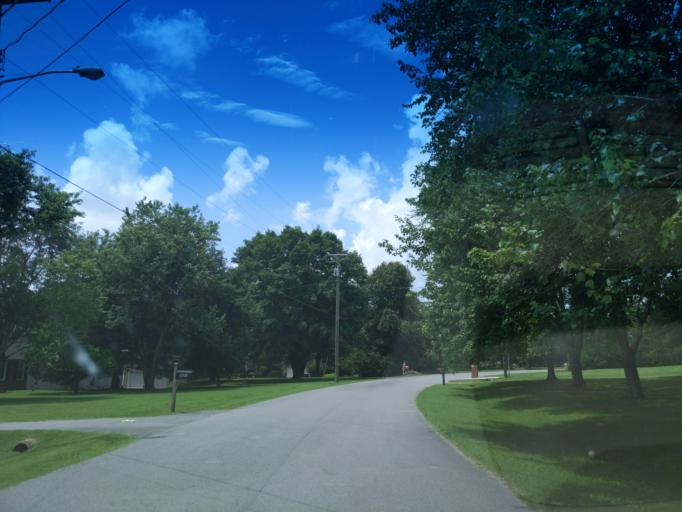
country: US
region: Tennessee
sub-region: Williamson County
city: Brentwood Estates
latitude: 36.0179
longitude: -86.7762
